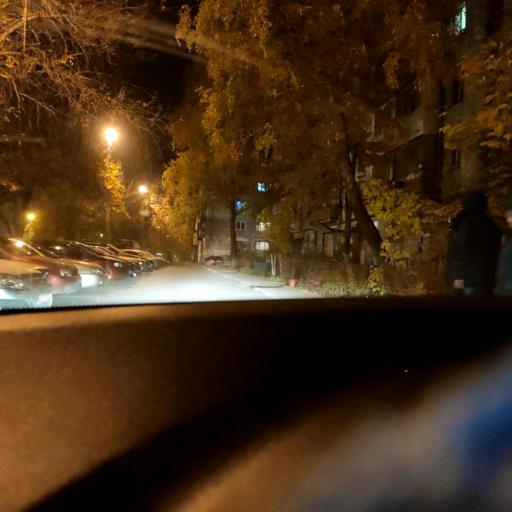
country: RU
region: Samara
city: Smyshlyayevka
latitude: 53.2273
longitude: 50.2915
